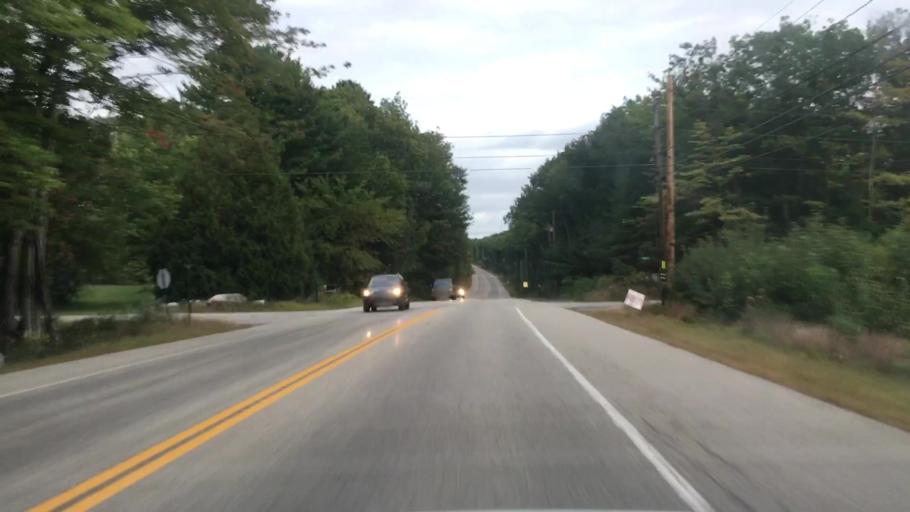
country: US
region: Maine
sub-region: York County
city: Alfred
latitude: 43.4763
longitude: -70.6744
